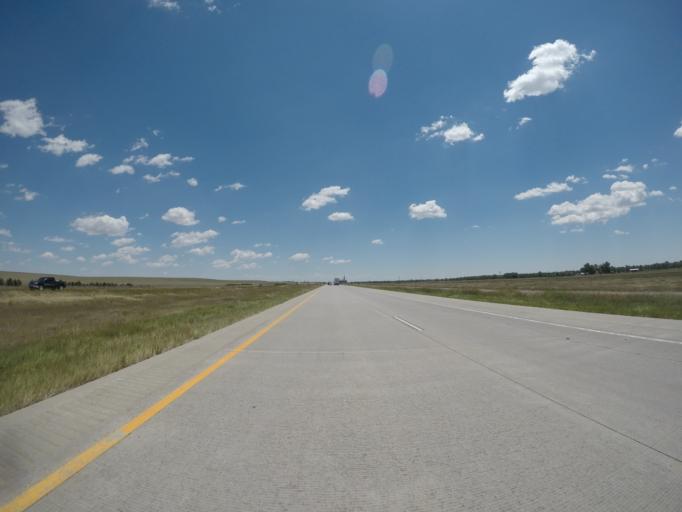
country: US
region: Colorado
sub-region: Lincoln County
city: Limon
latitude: 39.2751
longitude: -103.7441
